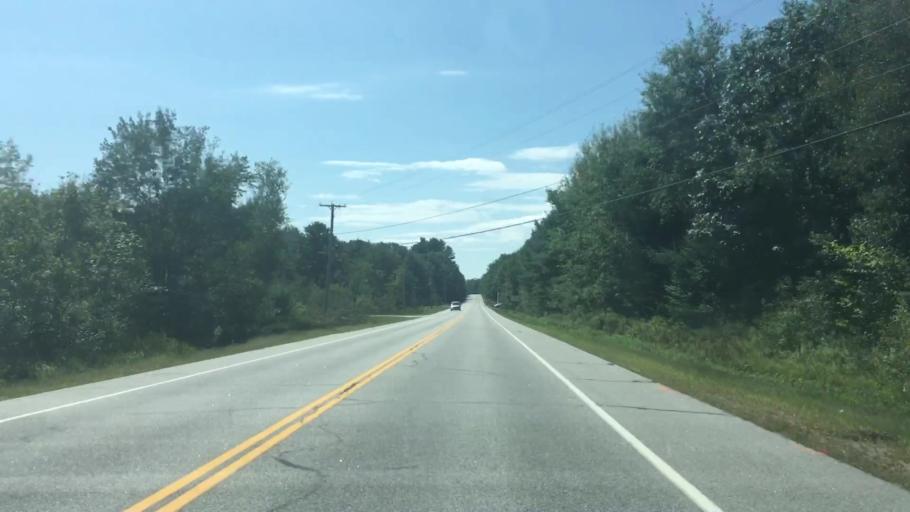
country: US
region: Maine
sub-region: Androscoggin County
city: Sabattus
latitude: 44.1399
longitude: -70.0515
